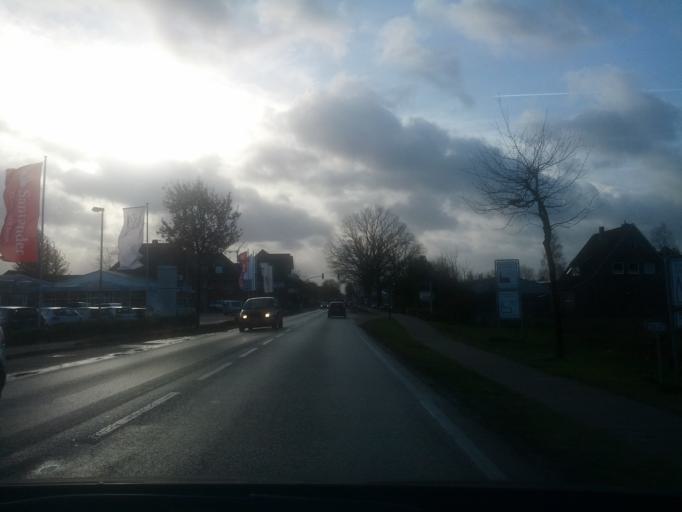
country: DE
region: Lower Saxony
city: Sittensen
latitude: 53.2878
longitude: 9.5066
